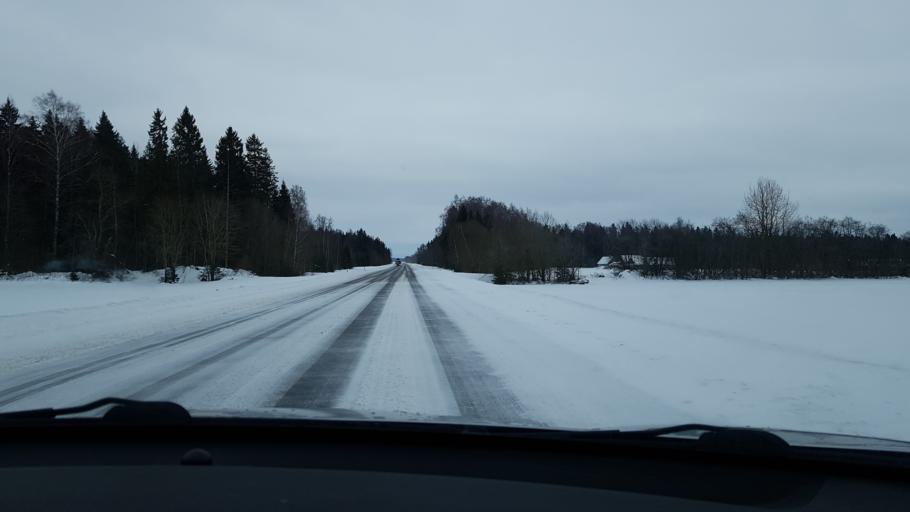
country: EE
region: Jaervamaa
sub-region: Jaerva-Jaani vald
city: Jarva-Jaani
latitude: 59.1359
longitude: 25.7740
